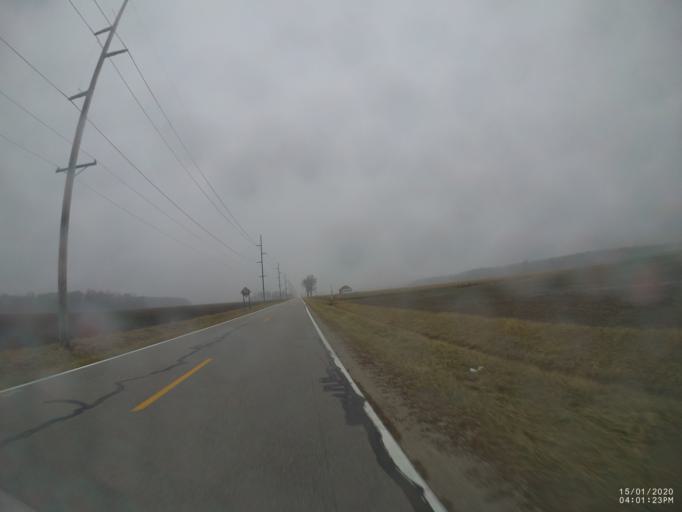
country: US
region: Ohio
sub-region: Sandusky County
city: Woodville
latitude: 41.4137
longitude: -83.3594
